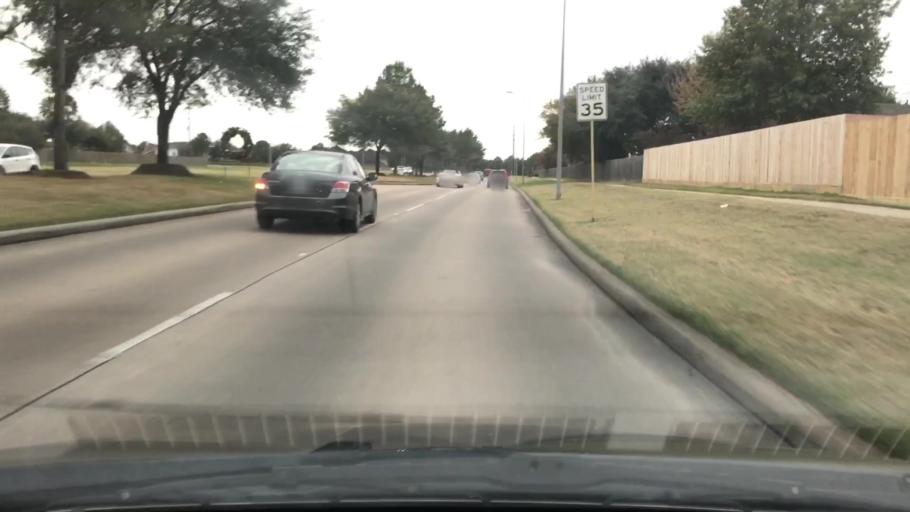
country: US
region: Texas
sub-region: Fort Bend County
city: Cinco Ranch
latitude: 29.7560
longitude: -95.7811
